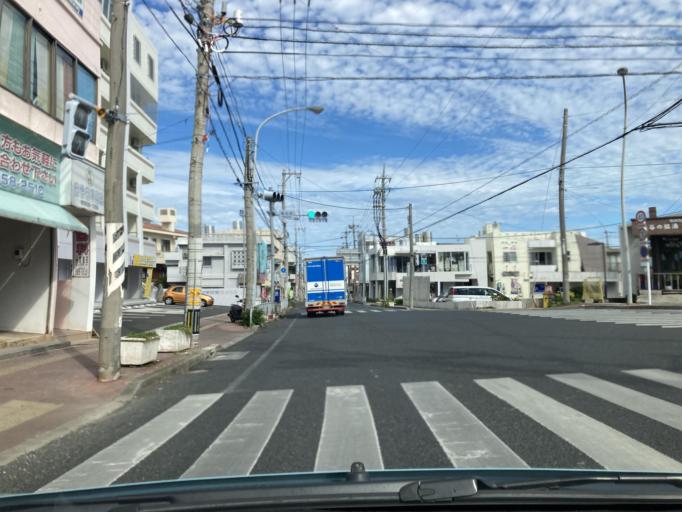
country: JP
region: Okinawa
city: Ishikawa
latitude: 26.4080
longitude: 127.7322
